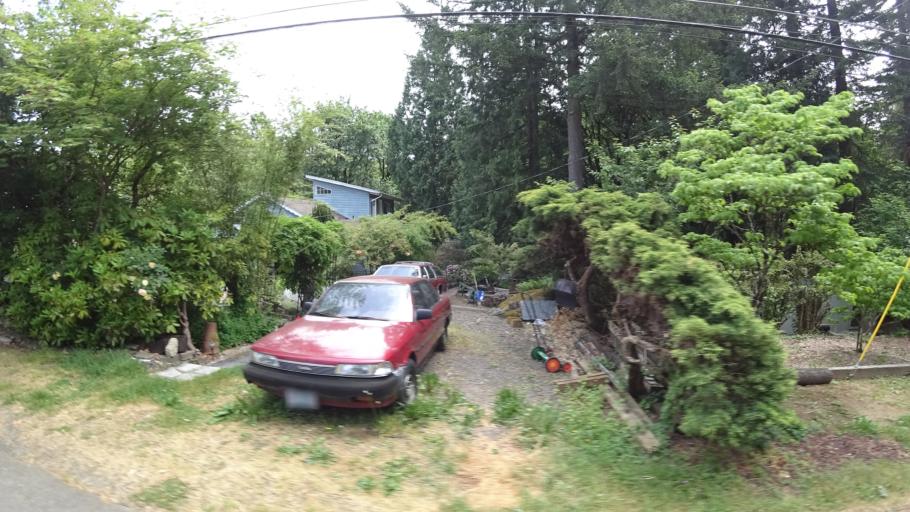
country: US
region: Oregon
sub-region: Clackamas County
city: Lake Oswego
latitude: 45.4466
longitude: -122.6834
